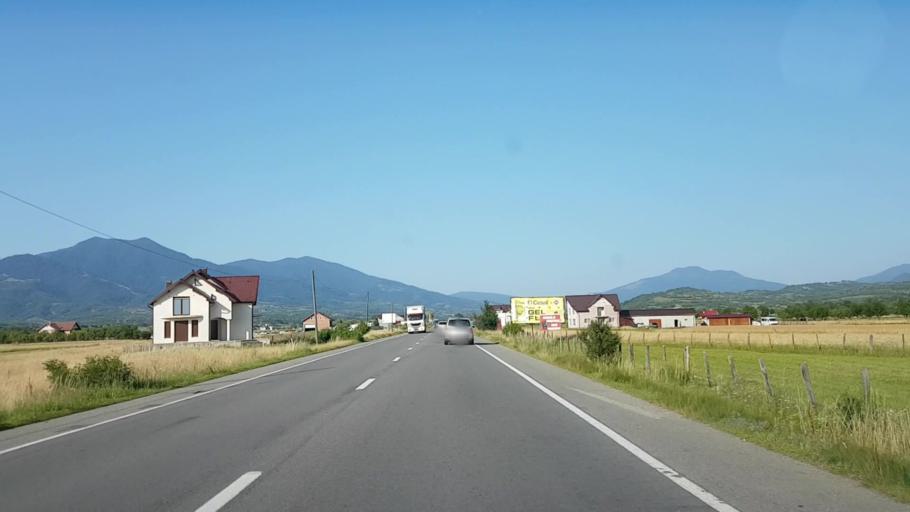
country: RO
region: Bistrita-Nasaud
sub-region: Comuna Josenii Bargaului
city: Josenii Bargaului
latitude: 47.2030
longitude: 24.6477
